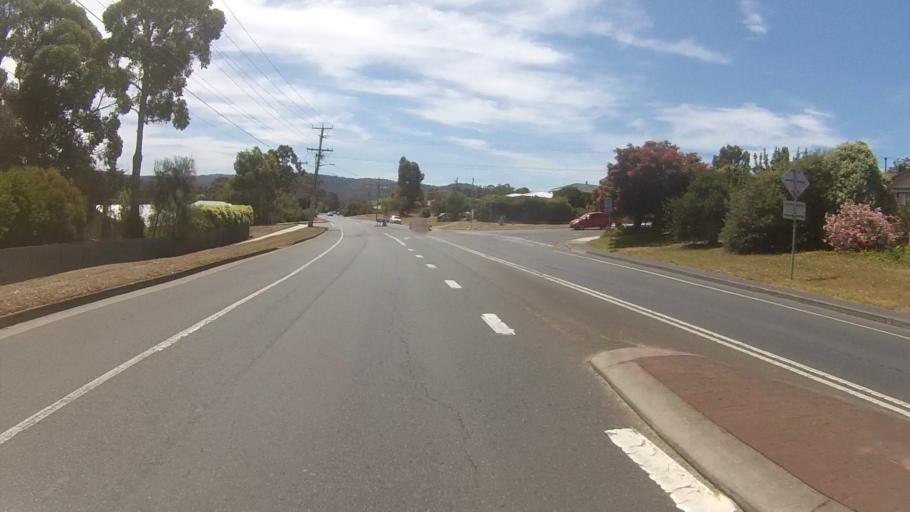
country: AU
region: Tasmania
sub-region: Kingborough
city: Kingston
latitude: -42.9818
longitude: 147.2970
